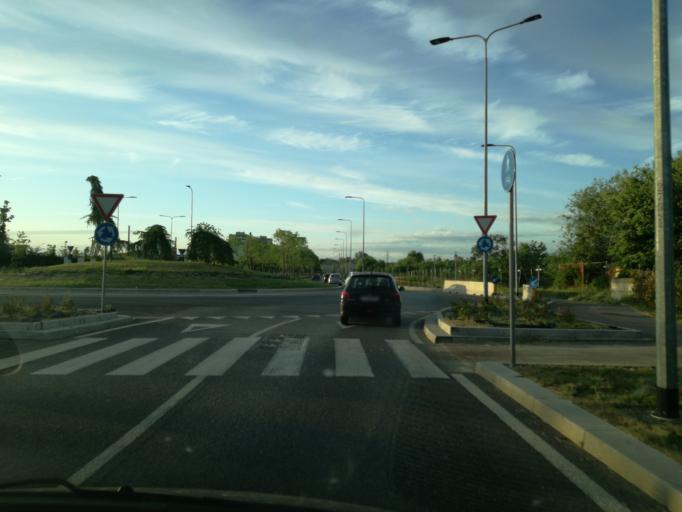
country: IT
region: Lombardy
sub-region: Citta metropolitana di Milano
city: Noverasco-Sporting Mirasole
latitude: 45.4158
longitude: 9.2060
